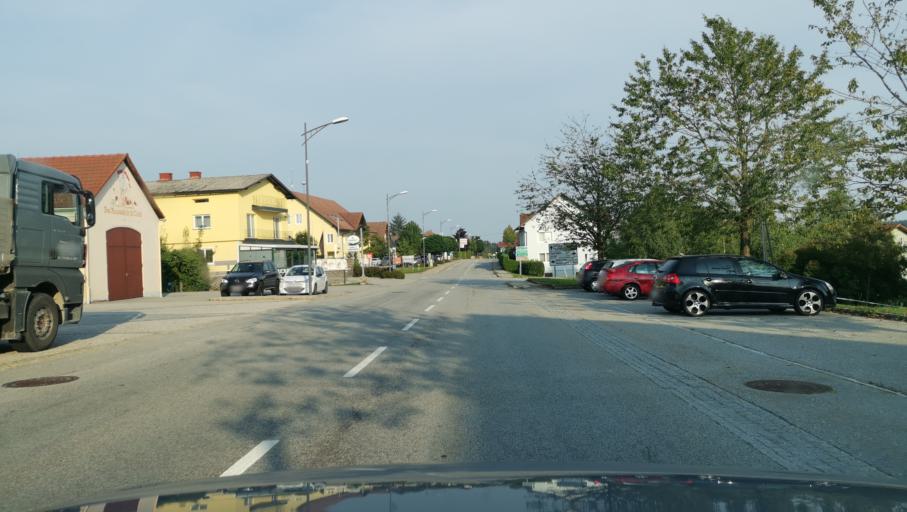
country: AT
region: Upper Austria
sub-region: Politischer Bezirk Grieskirchen
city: Grieskirchen
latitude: 48.3606
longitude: 13.6883
